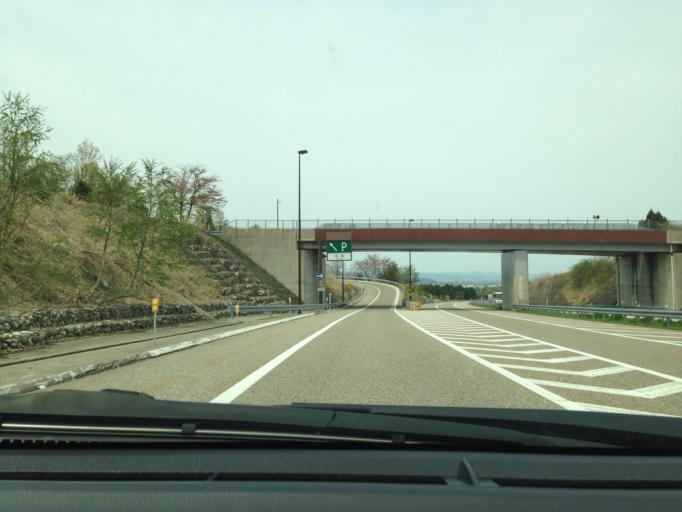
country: JP
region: Toyama
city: Fukumitsu
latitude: 36.5025
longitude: 136.8741
